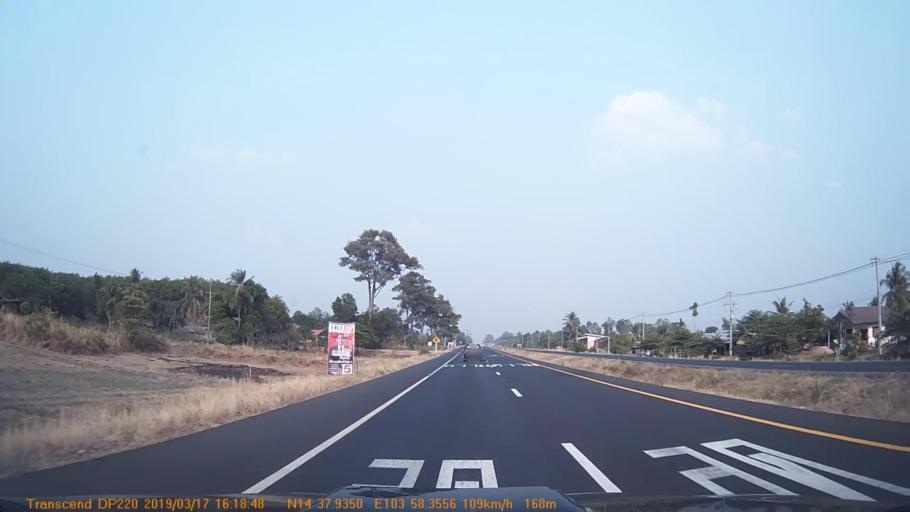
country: TH
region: Surin
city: Bua Chet
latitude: 14.6323
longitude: 103.9728
